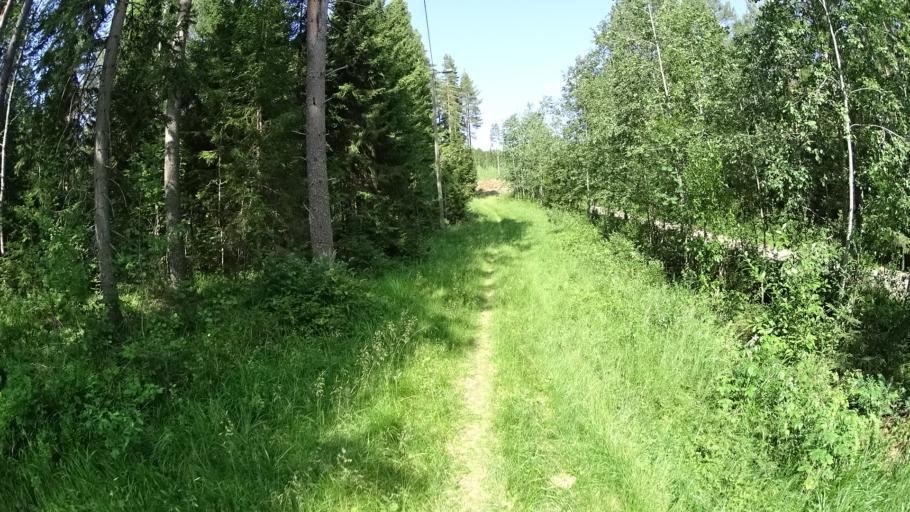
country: FI
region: North Karelia
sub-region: Pielisen Karjala
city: Lieksa
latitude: 63.1236
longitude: 29.8053
